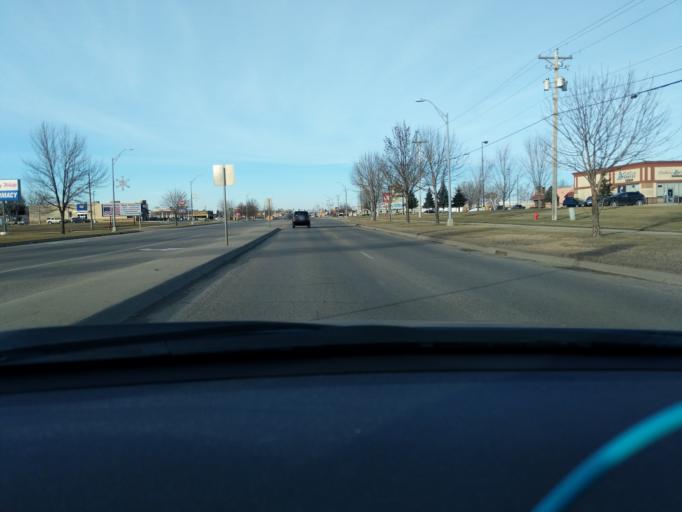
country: US
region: Minnesota
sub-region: Kandiyohi County
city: Willmar
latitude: 45.0995
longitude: -95.0426
